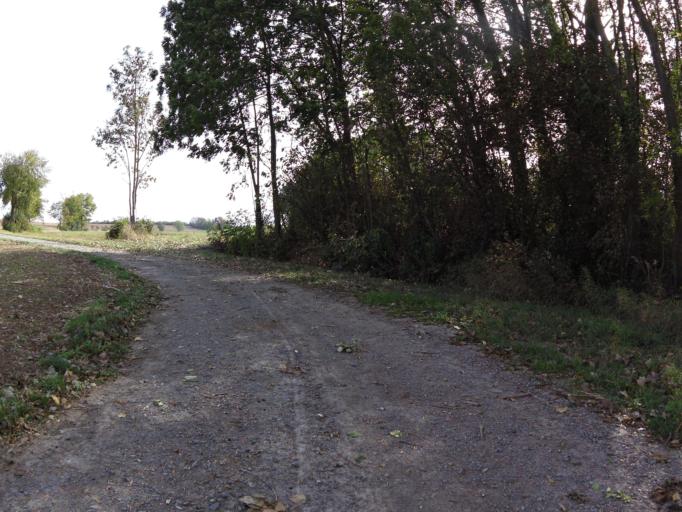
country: DE
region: Bavaria
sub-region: Regierungsbezirk Unterfranken
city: Reichenberg
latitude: 49.7007
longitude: 9.9490
